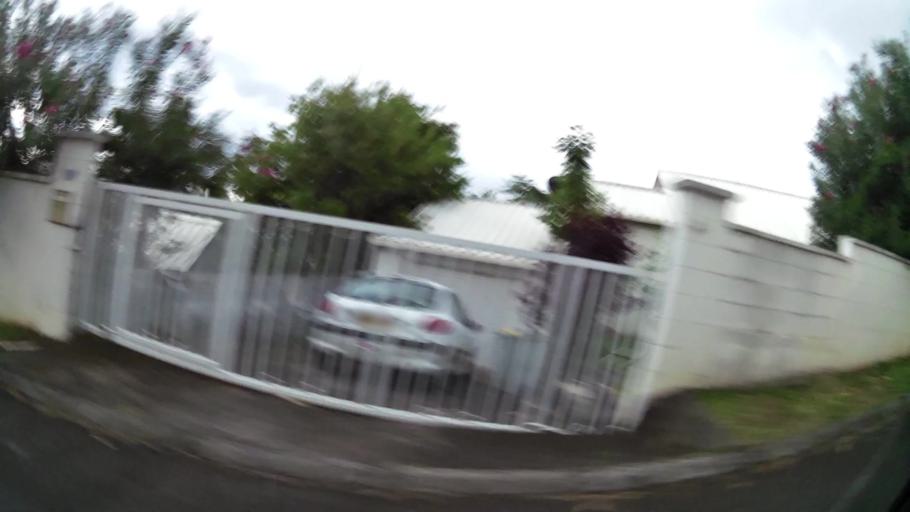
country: RE
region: Reunion
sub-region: Reunion
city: Saint-Denis
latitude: -20.9094
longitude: 55.4670
